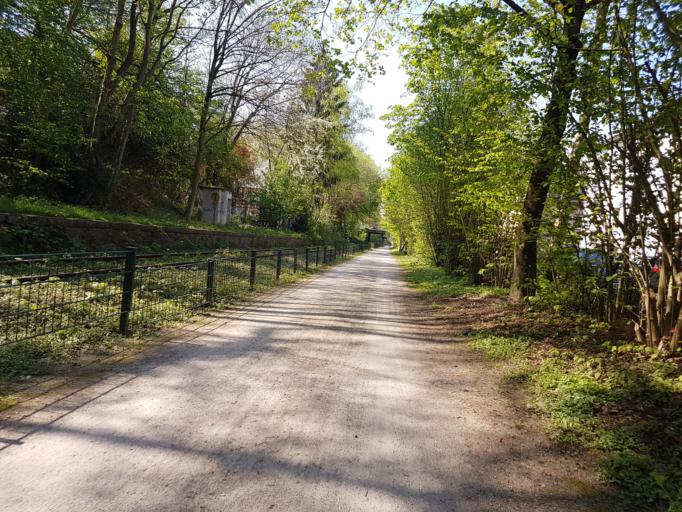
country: DE
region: North Rhine-Westphalia
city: Witten
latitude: 51.4249
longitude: 7.3394
